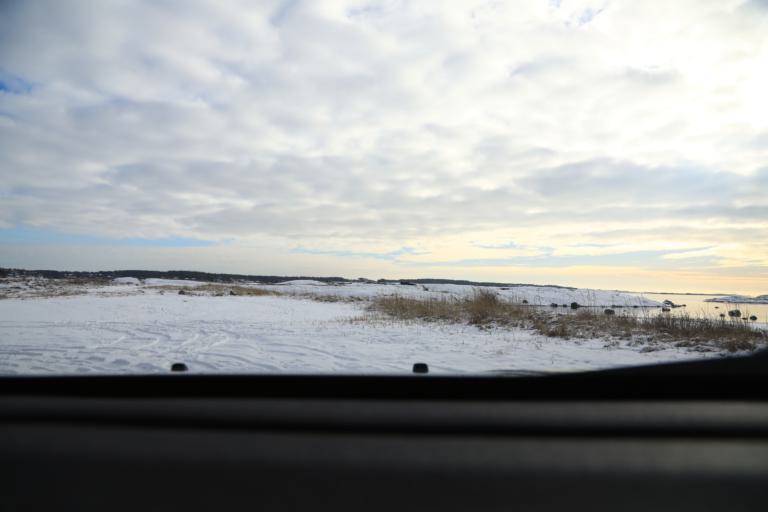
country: SE
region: Halland
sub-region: Kungsbacka Kommun
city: Frillesas
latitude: 57.2154
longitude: 12.1706
